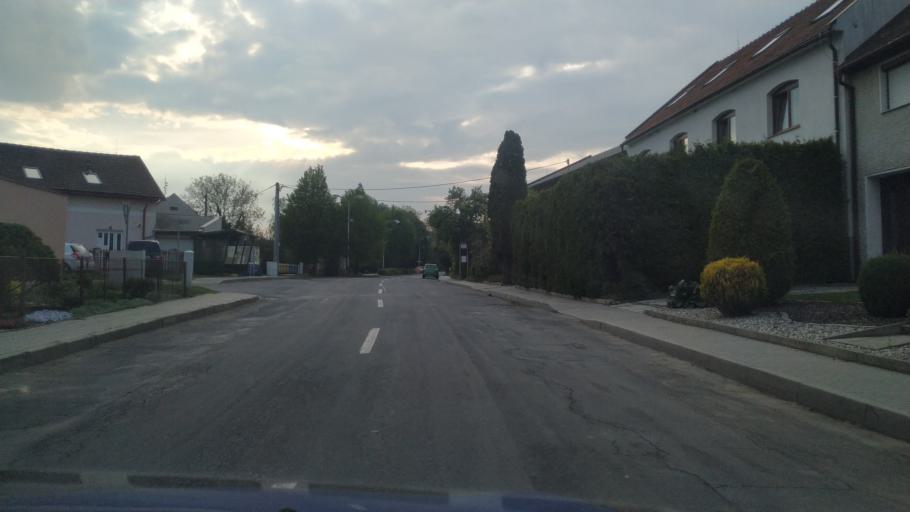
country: CZ
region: Olomoucky
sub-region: Okres Olomouc
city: Slatinice
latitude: 49.5509
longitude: 17.1115
